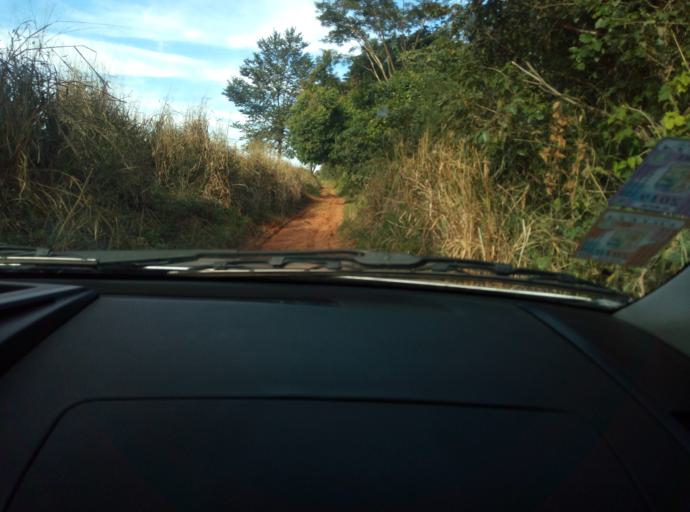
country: PY
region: Caaguazu
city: Carayao
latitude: -25.1730
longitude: -56.2816
